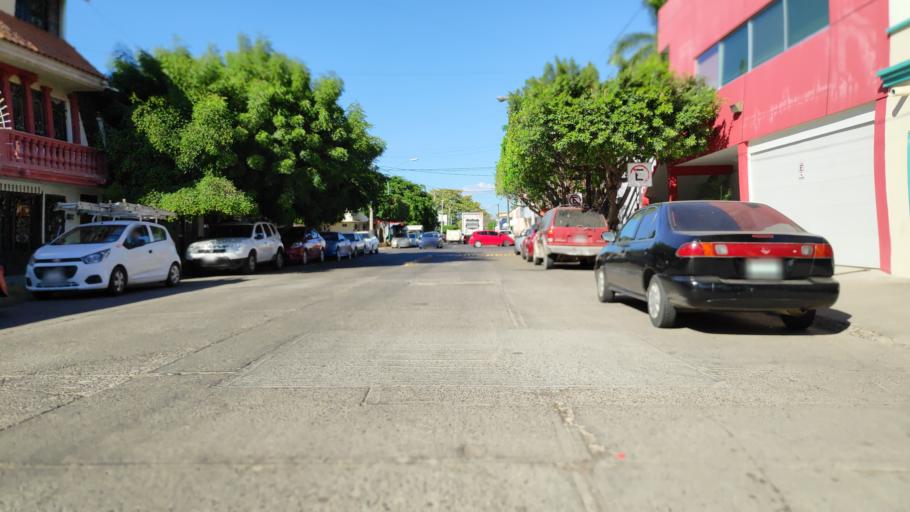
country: MX
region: Sinaloa
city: Culiacan
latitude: 24.7977
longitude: -107.3964
